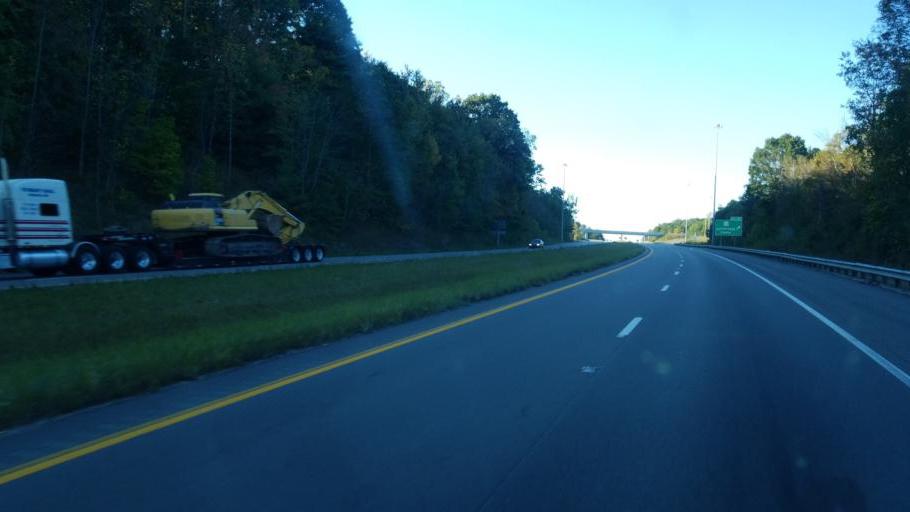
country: US
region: Ohio
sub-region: Guernsey County
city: Cambridge
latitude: 40.0447
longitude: -81.5611
